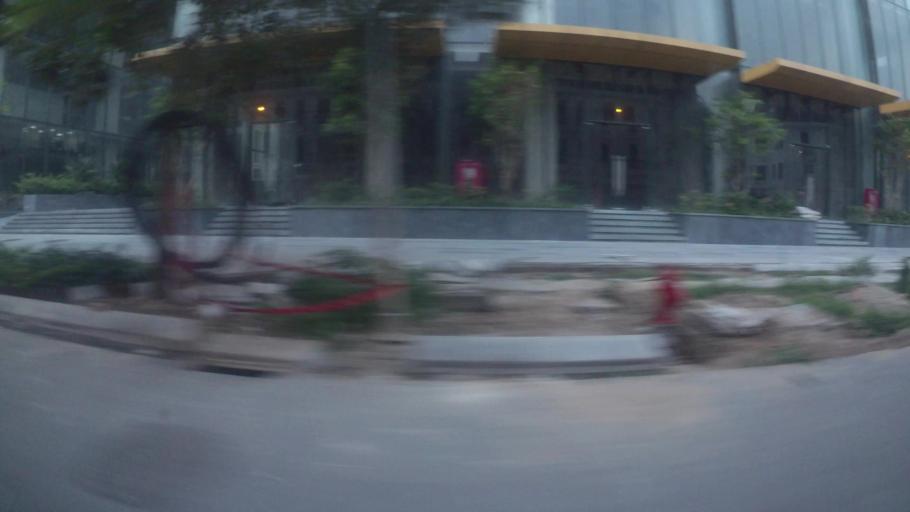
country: VN
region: Ha Noi
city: Tay Ho
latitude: 21.0642
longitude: 105.7986
